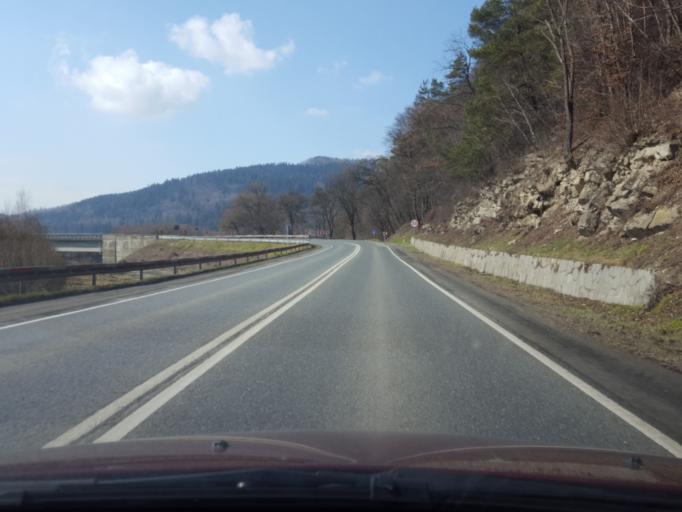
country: PL
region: Lesser Poland Voivodeship
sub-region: Powiat nowosadecki
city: Lososina Dolna
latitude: 49.6929
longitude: 20.6559
